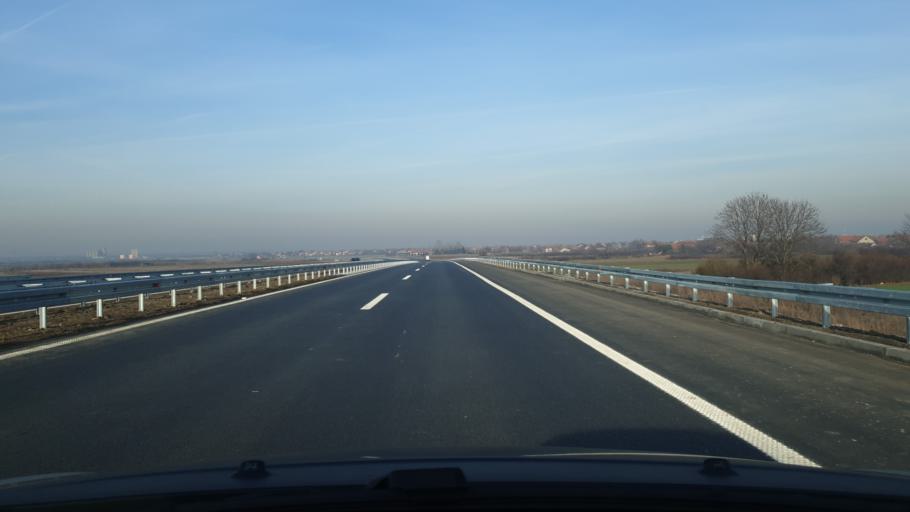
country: RS
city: Boljevci
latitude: 44.7438
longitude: 20.2492
